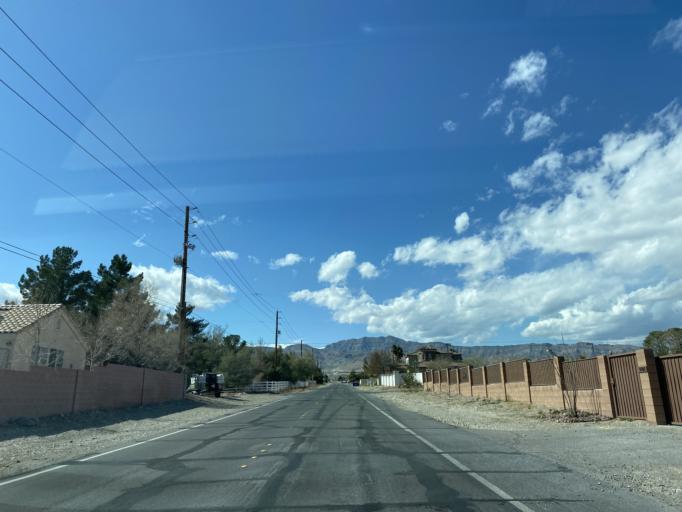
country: US
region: Nevada
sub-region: Clark County
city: Summerlin South
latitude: 36.2556
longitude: -115.2943
